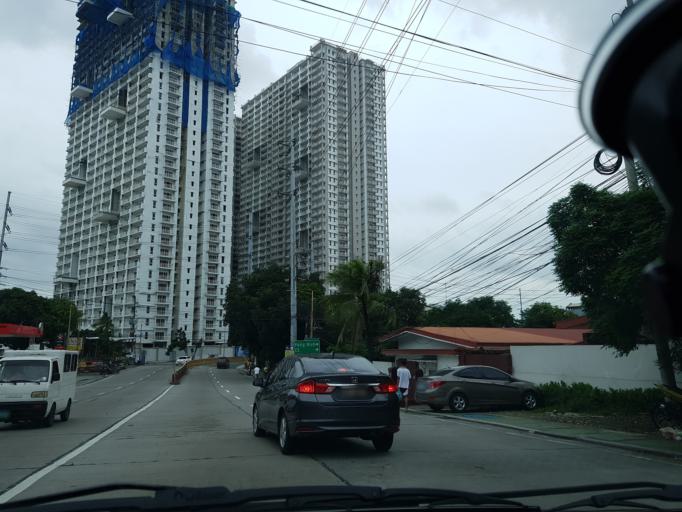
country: PH
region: Metro Manila
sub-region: Pasig
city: Pasig City
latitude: 14.5709
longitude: 121.0657
